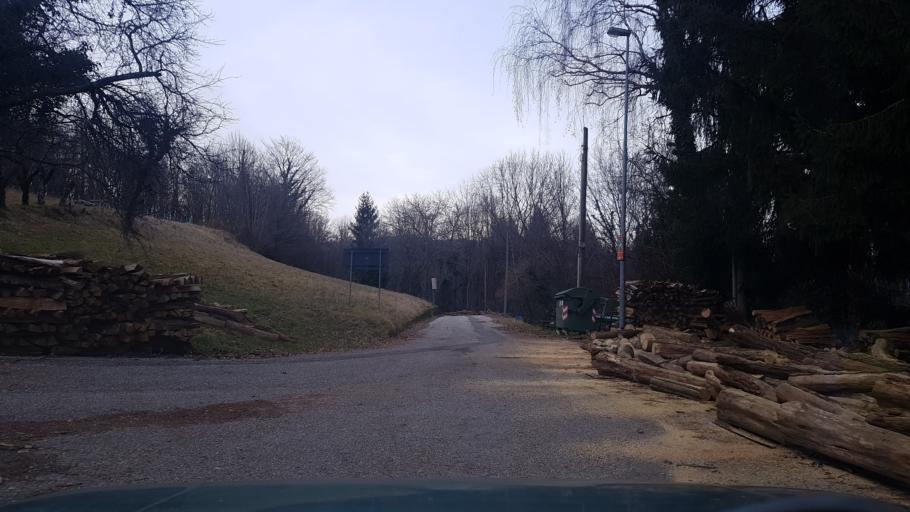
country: IT
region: Friuli Venezia Giulia
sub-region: Provincia di Udine
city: San Pietro al Natisone
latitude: 46.1427
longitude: 13.4633
